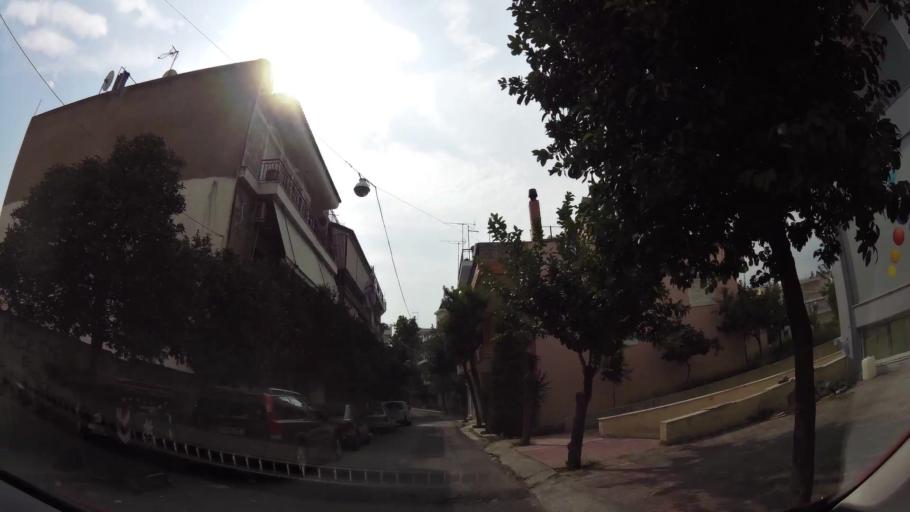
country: GR
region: Attica
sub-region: Nomarchia Athinas
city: Chaidari
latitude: 38.0133
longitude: 23.6750
